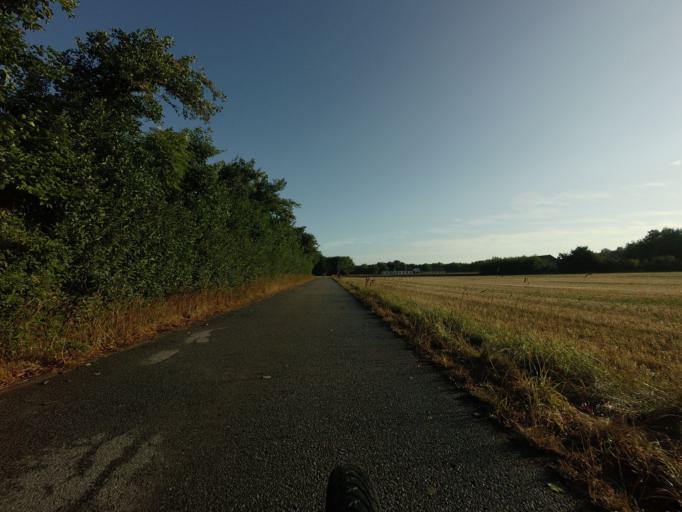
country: DK
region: North Denmark
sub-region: Hjorring Kommune
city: Vra
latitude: 57.3610
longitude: 9.8659
